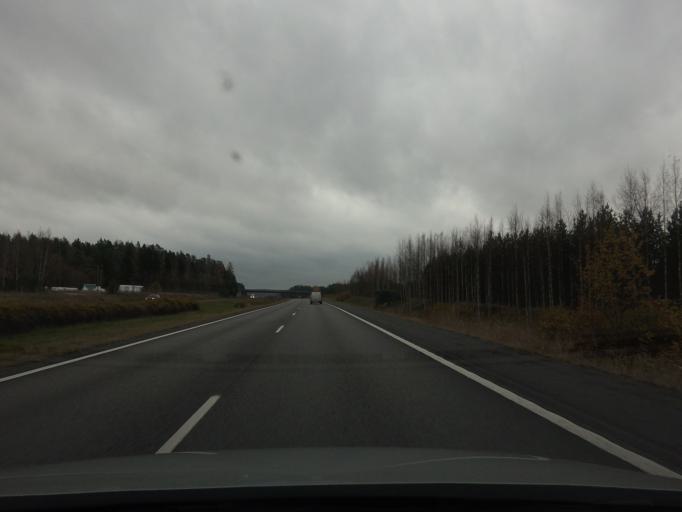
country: FI
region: Varsinais-Suomi
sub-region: Turku
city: Paimio
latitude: 60.4380
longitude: 22.6294
